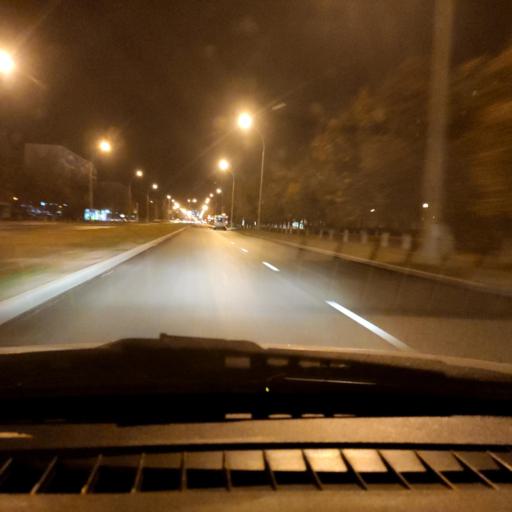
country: RU
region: Samara
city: Tol'yatti
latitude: 53.5369
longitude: 49.3294
